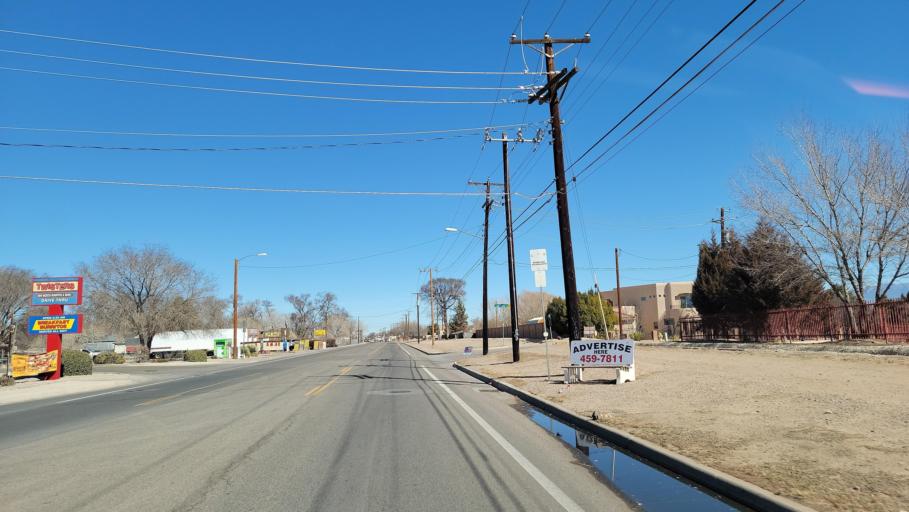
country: US
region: New Mexico
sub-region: Bernalillo County
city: South Valley
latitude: 35.0142
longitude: -106.6858
